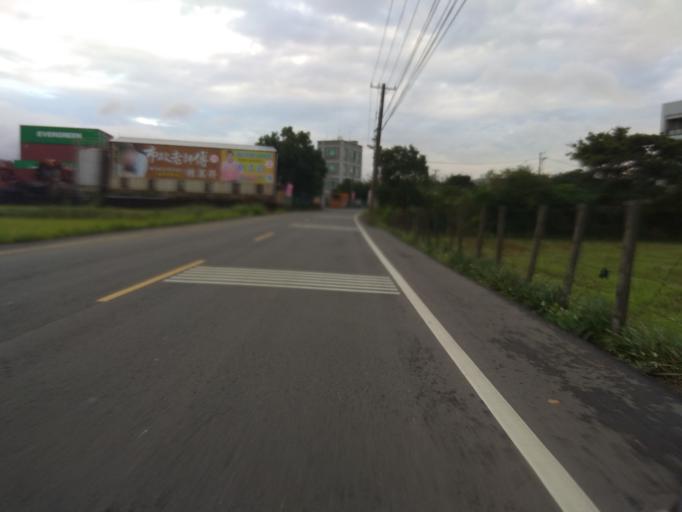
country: TW
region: Taiwan
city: Taoyuan City
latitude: 24.9483
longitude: 121.1909
